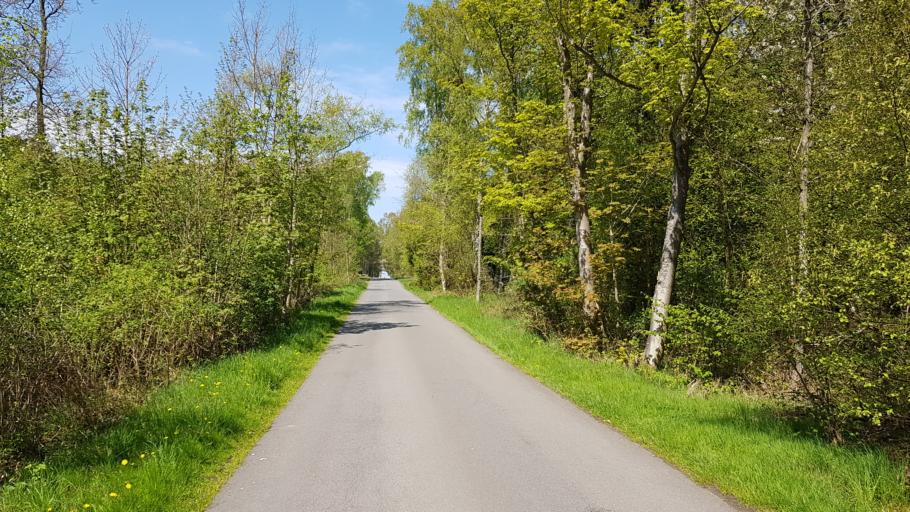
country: DK
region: Capital Region
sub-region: Bornholm Kommune
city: Nexo
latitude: 54.9992
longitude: 15.0844
